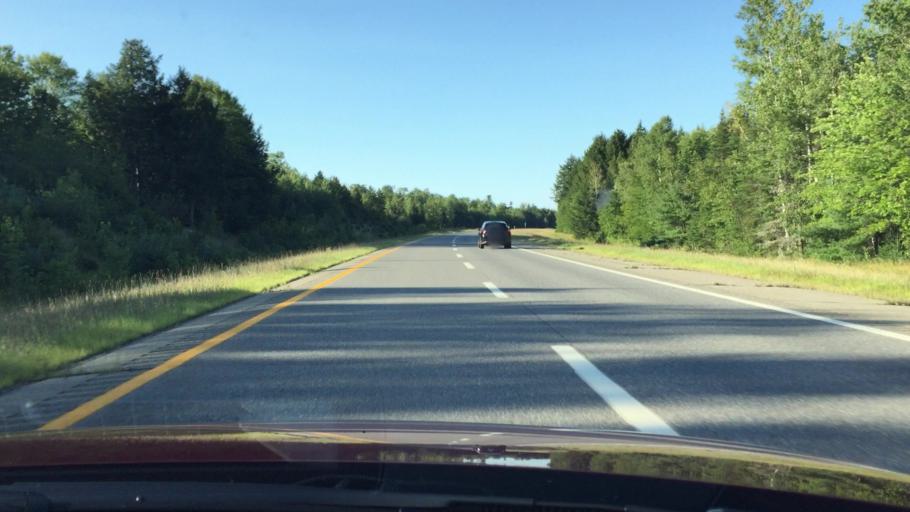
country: US
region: Maine
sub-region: Penobscot County
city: Lincoln
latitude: 45.4511
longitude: -68.5908
